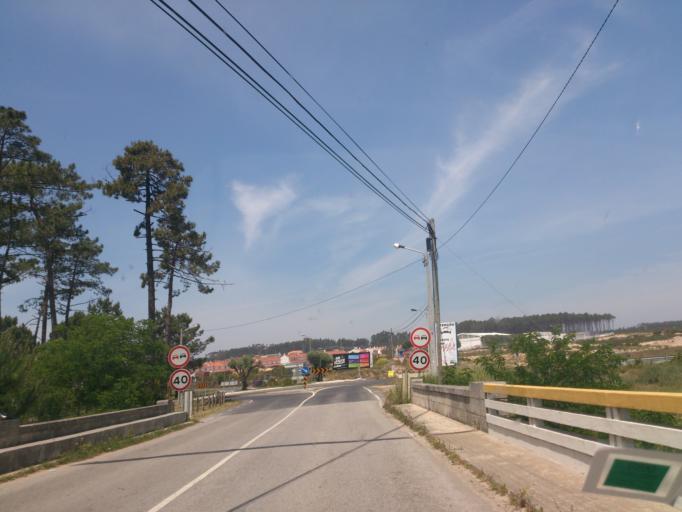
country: PT
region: Leiria
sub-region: Alcobaca
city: Alcobaca
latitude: 39.5867
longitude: -9.0143
